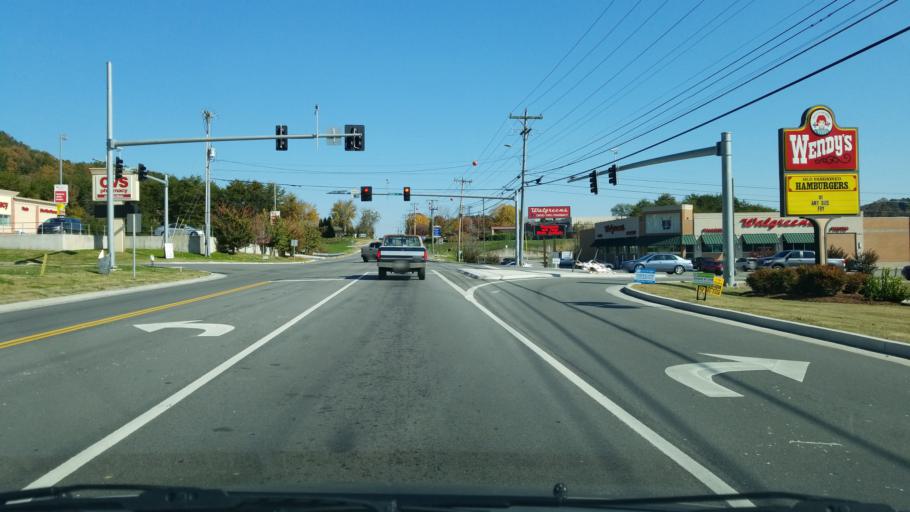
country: US
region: Tennessee
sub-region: Hamilton County
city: Soddy-Daisy
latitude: 35.2368
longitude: -85.1995
